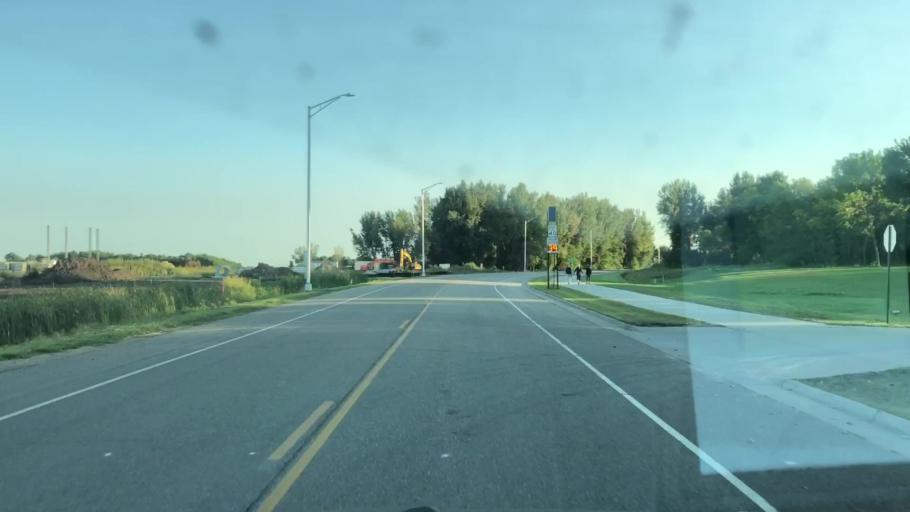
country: US
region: Minnesota
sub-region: Nobles County
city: Worthington
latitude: 43.6219
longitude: -95.6335
